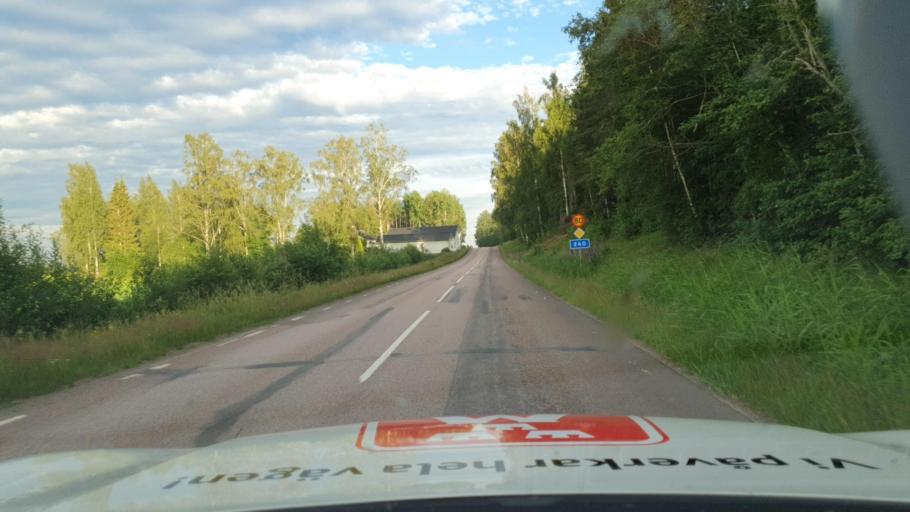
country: SE
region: Vaermland
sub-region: Karlstads Kommun
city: Molkom
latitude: 59.4519
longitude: 13.8308
